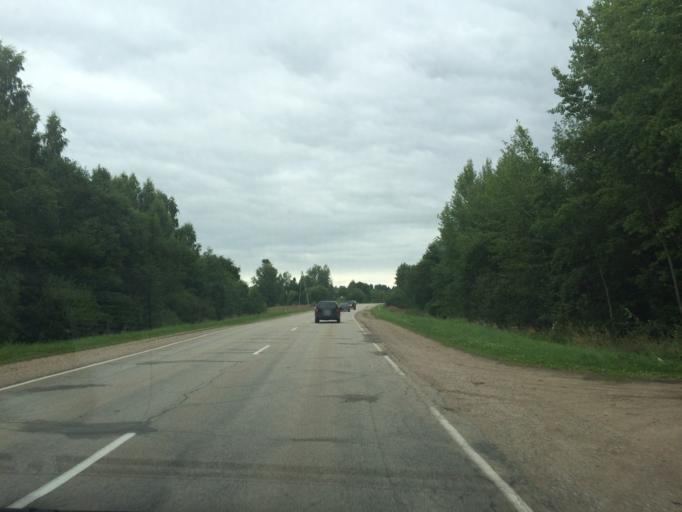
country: LV
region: Rezekne
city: Rezekne
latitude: 56.5674
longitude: 27.3681
